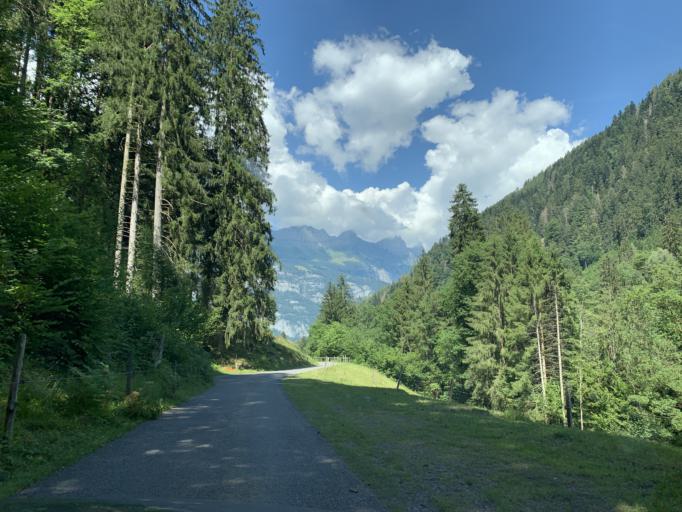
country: CH
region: Saint Gallen
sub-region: Wahlkreis Sarganserland
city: Quarten
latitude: 47.0965
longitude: 9.2097
